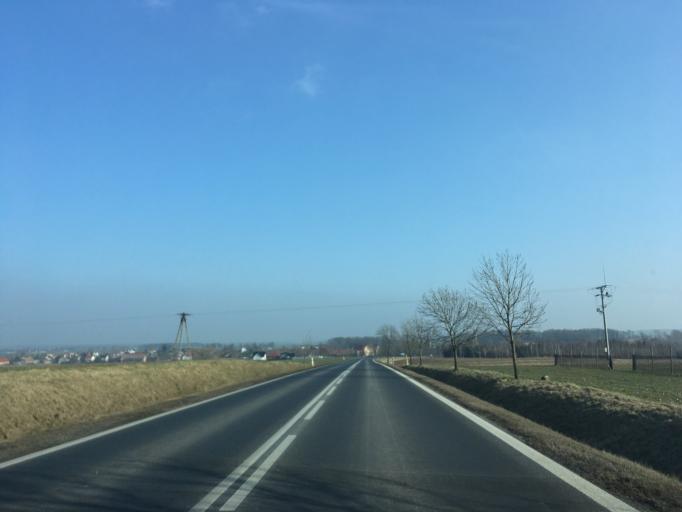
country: PL
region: Lower Silesian Voivodeship
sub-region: Powiat boleslawiecki
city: Boleslawiec
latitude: 51.2606
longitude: 15.6692
